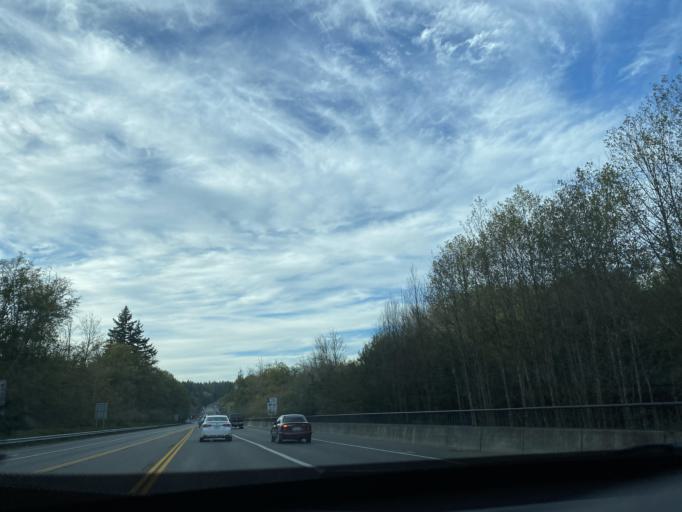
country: US
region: Washington
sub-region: Kitsap County
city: Poulsbo
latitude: 47.7481
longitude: -122.6407
